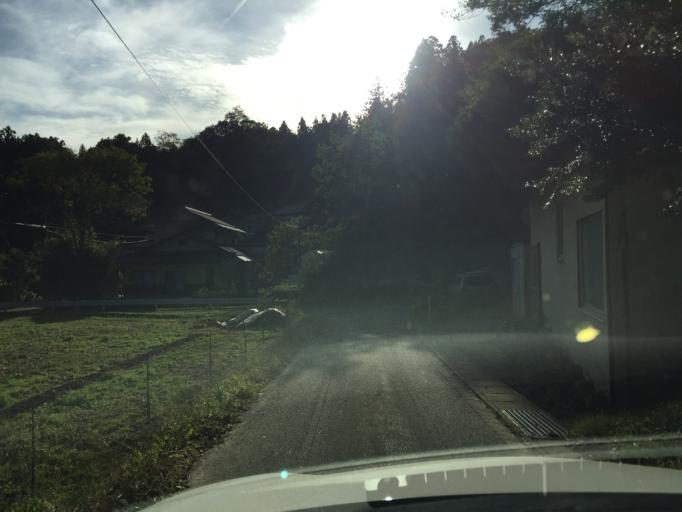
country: JP
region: Fukushima
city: Ishikawa
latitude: 37.2304
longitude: 140.6080
